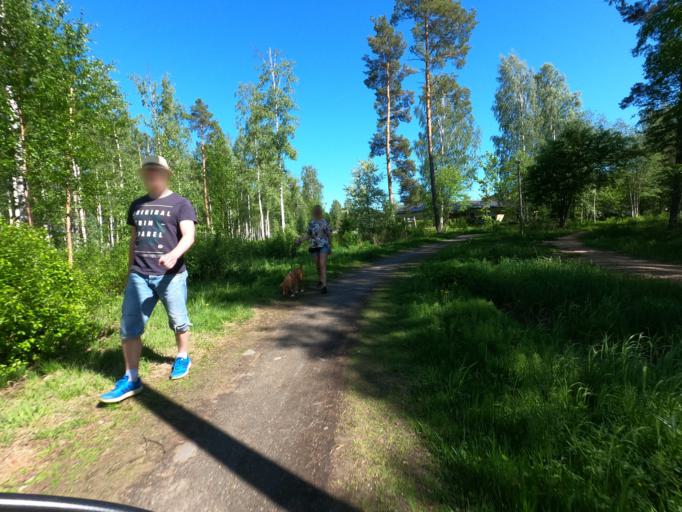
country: FI
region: North Karelia
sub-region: Joensuu
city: Joensuu
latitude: 62.6077
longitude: 29.7987
